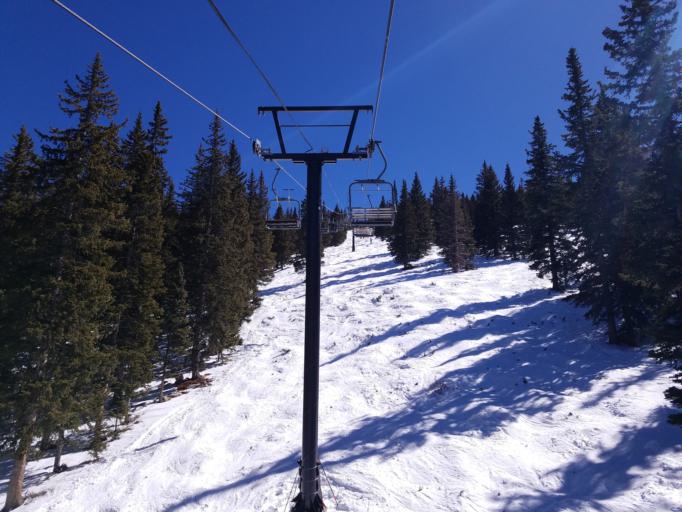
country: US
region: New Mexico
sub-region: Santa Fe County
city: Santa Fe
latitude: 35.7894
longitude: -105.7882
